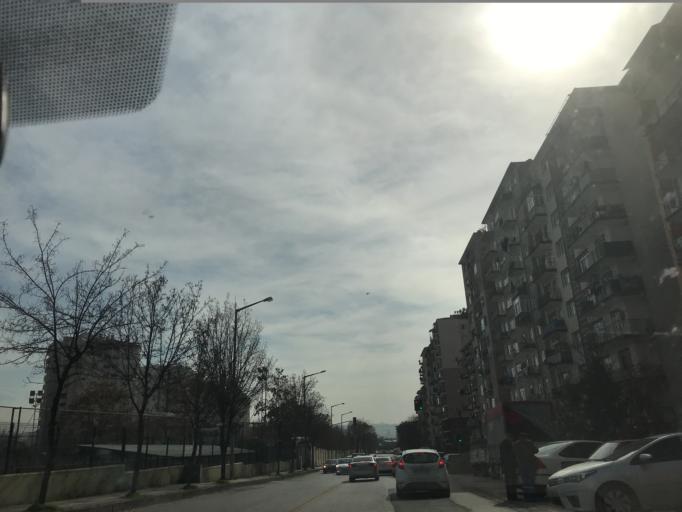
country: TR
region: Ankara
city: Batikent
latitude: 39.9618
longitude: 32.7969
